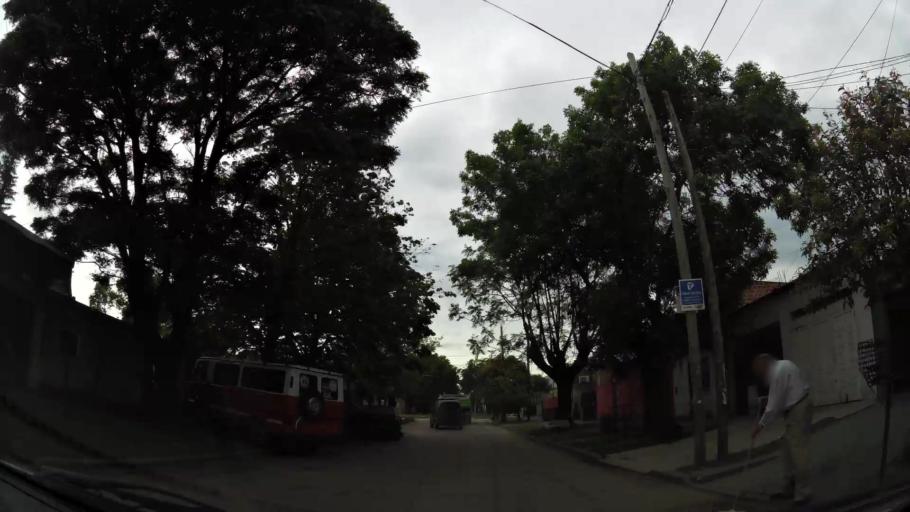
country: AR
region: Buenos Aires
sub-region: Partido de Quilmes
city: Quilmes
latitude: -34.7990
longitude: -58.2734
